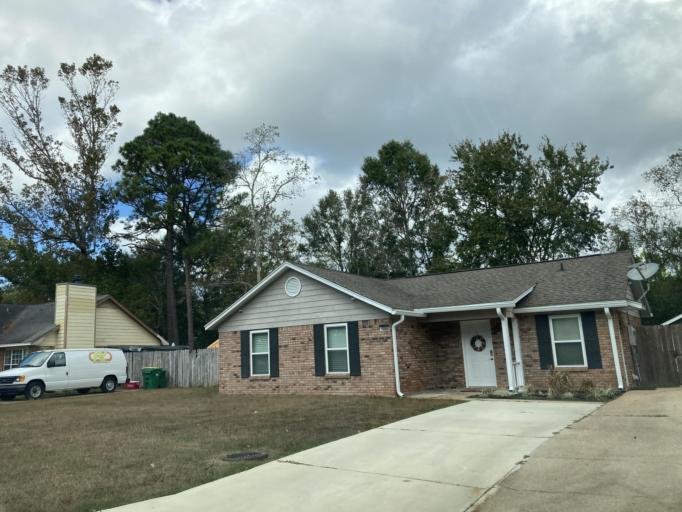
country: US
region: Mississippi
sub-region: Jackson County
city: Gulf Hills
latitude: 30.4470
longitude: -88.8264
